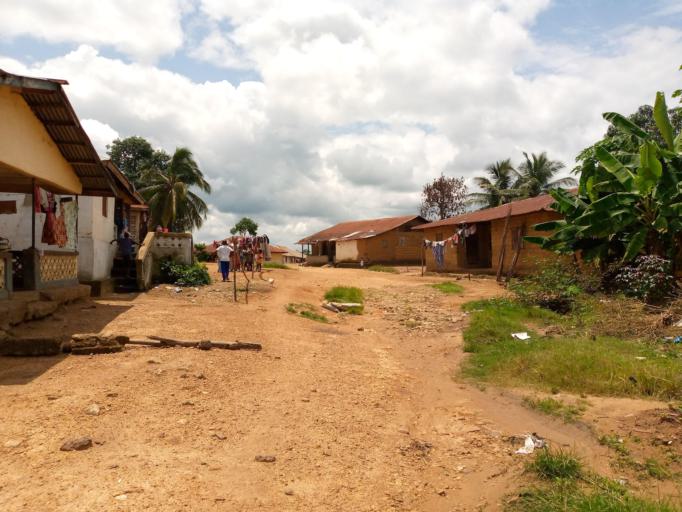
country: SL
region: Northern Province
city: Magburaka
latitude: 8.7310
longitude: -11.9443
